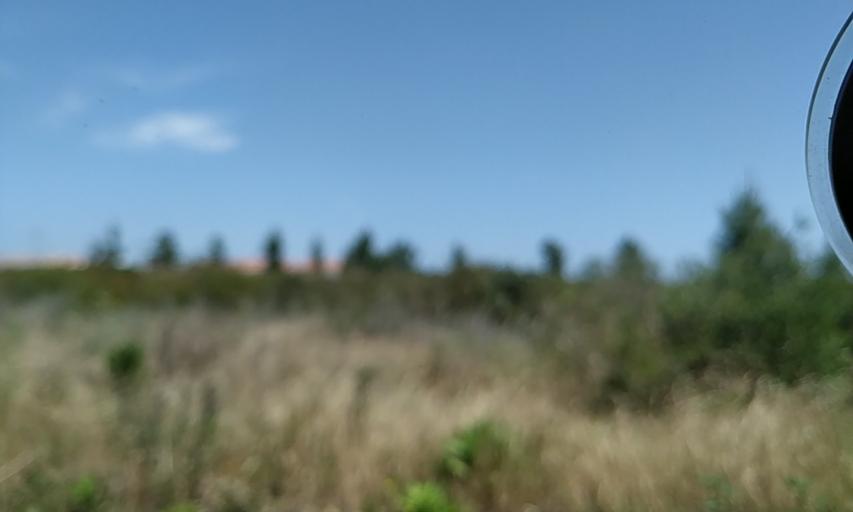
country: PT
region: Setubal
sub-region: Palmela
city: Palmela
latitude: 38.6307
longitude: -8.7467
